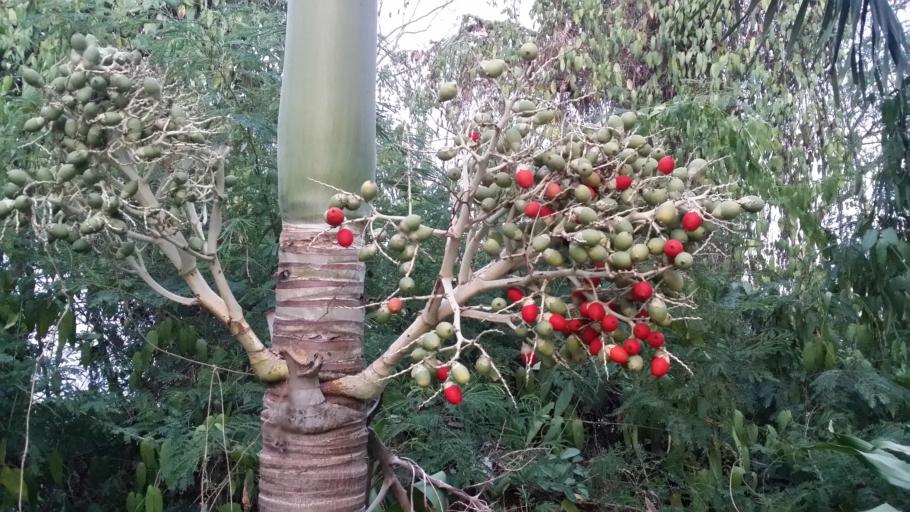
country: TH
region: Chon Buri
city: Phatthaya
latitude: 12.9158
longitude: 100.8686
